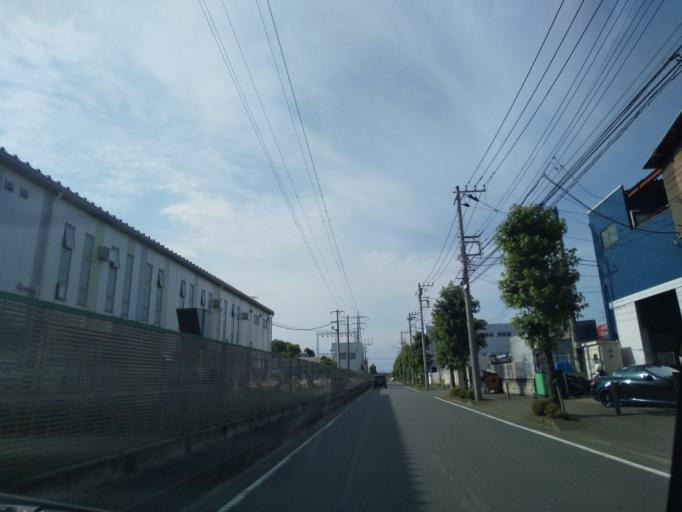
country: JP
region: Kanagawa
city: Zama
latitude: 35.4679
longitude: 139.3851
